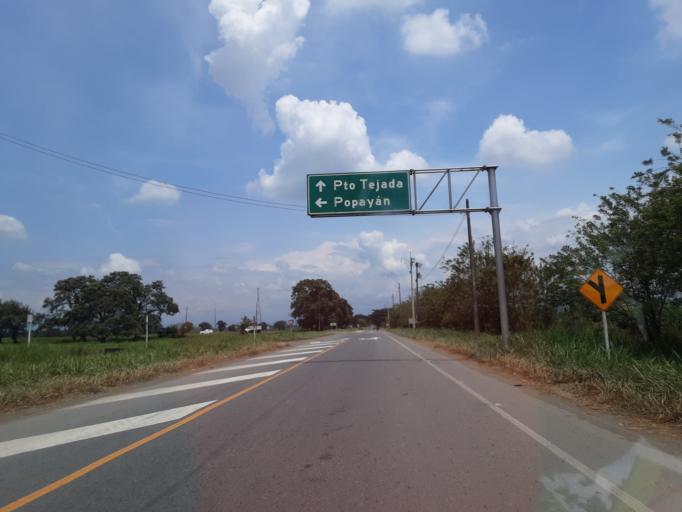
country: CO
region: Cauca
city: Puerto Tejada
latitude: 3.2340
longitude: -76.3935
